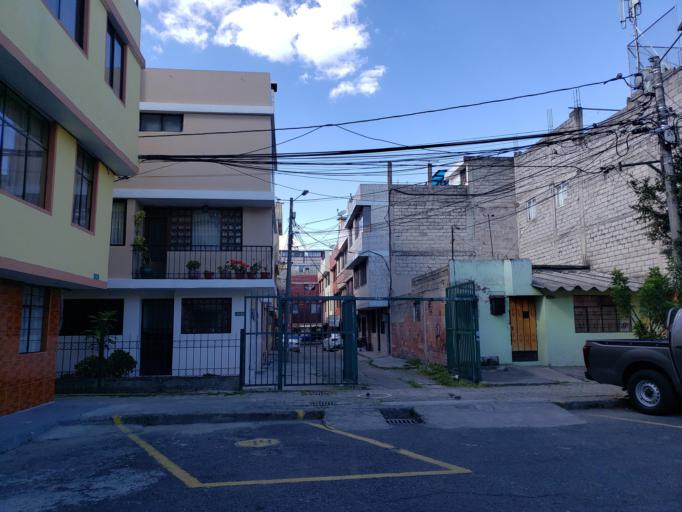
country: EC
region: Pichincha
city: Quito
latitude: -0.2684
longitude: -78.5367
